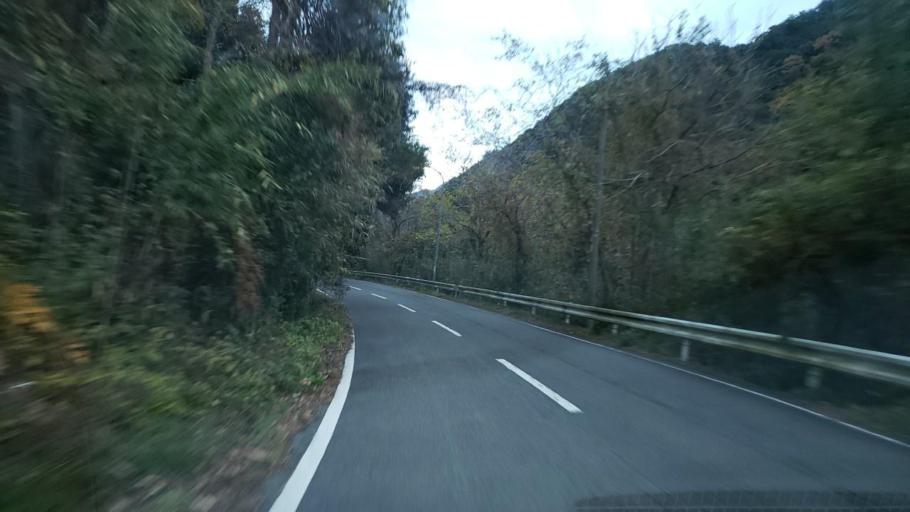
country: JP
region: Tokushima
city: Kamojimacho-jogejima
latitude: 34.1984
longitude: 134.2727
